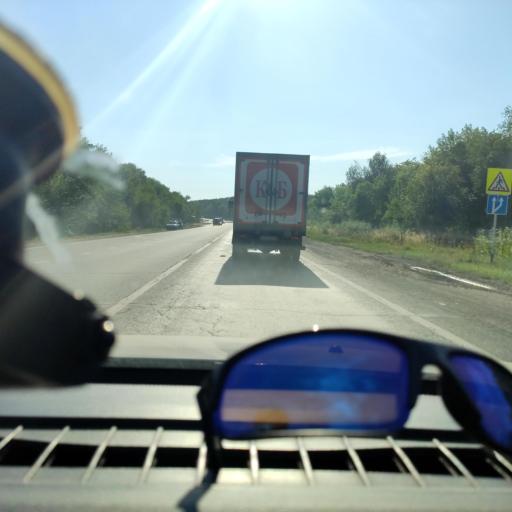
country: RU
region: Samara
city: Novokuybyshevsk
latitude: 52.9838
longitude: 49.8752
